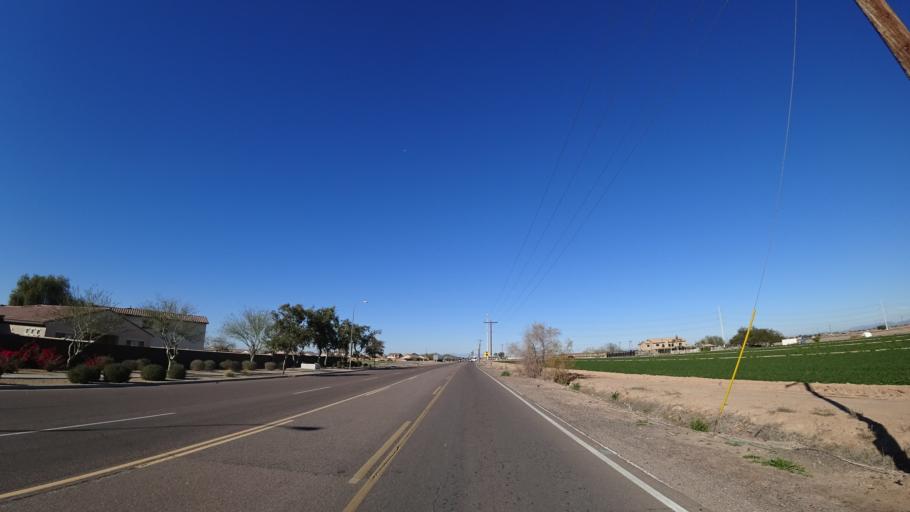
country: US
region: Arizona
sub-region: Maricopa County
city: Tolleson
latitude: 33.4040
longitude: -112.2722
